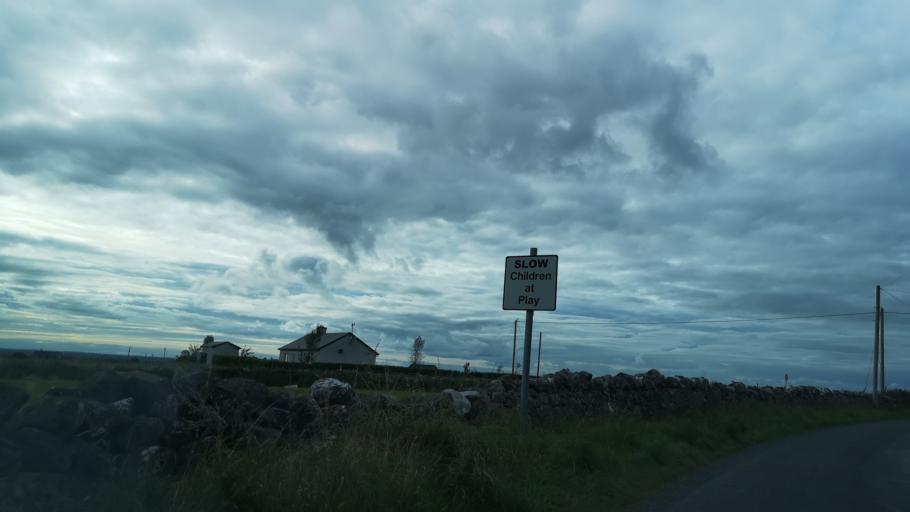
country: IE
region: Connaught
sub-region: County Galway
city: Ballinasloe
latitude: 53.3810
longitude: -8.1782
